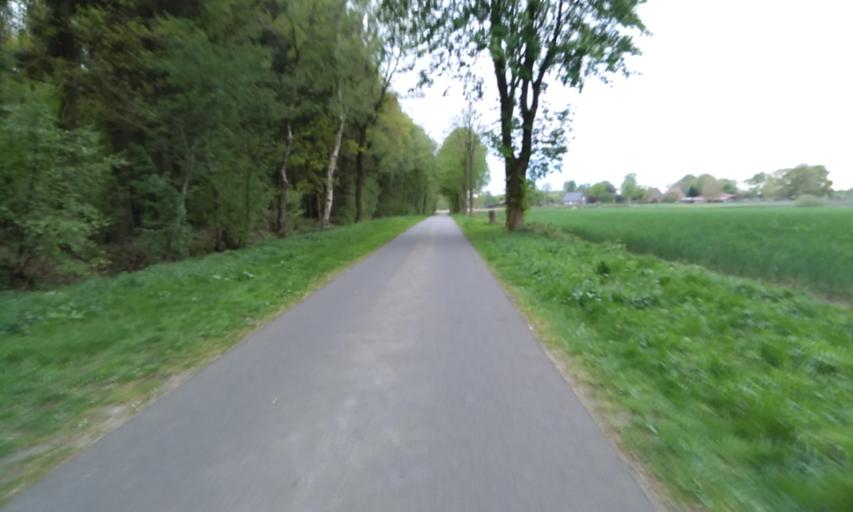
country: DE
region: Lower Saxony
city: Harsefeld
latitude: 53.4680
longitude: 9.4937
